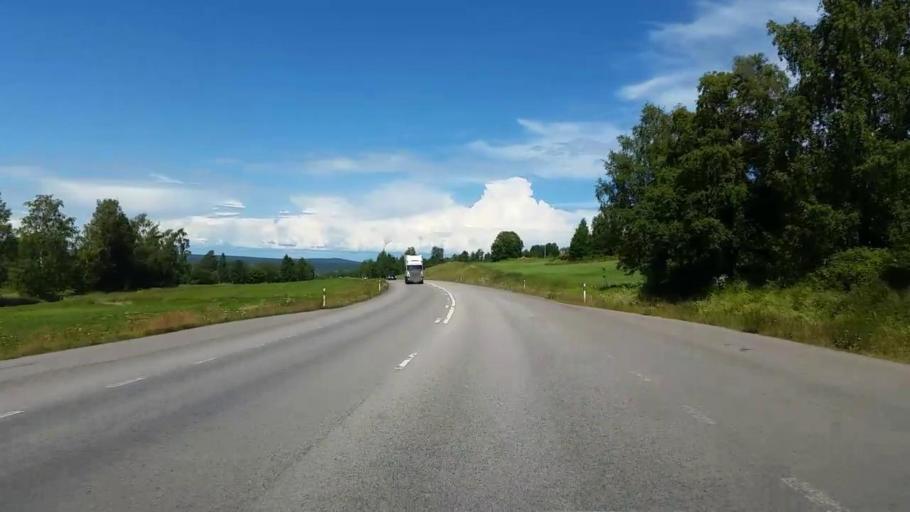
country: SE
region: Dalarna
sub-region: Rattviks Kommun
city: Raettvik
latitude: 60.8479
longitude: 15.1058
